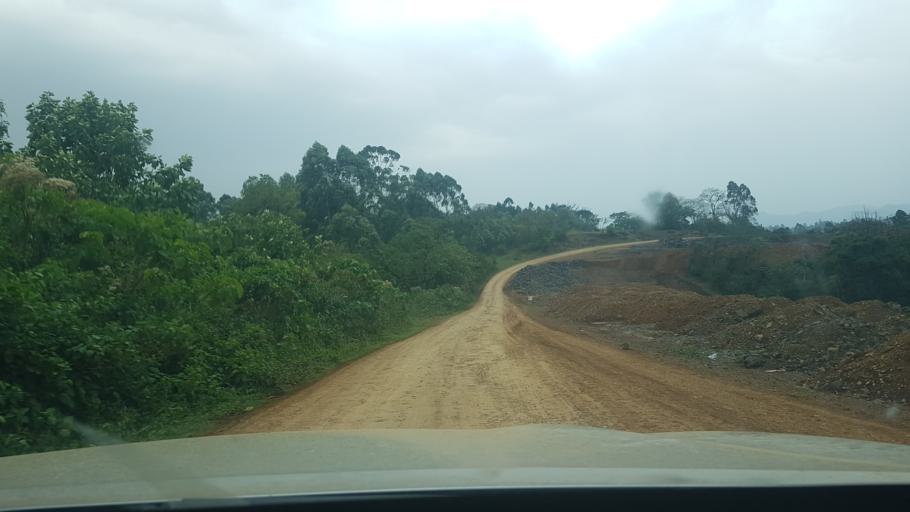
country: ET
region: Oromiya
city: Gore
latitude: 7.9186
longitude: 35.5144
